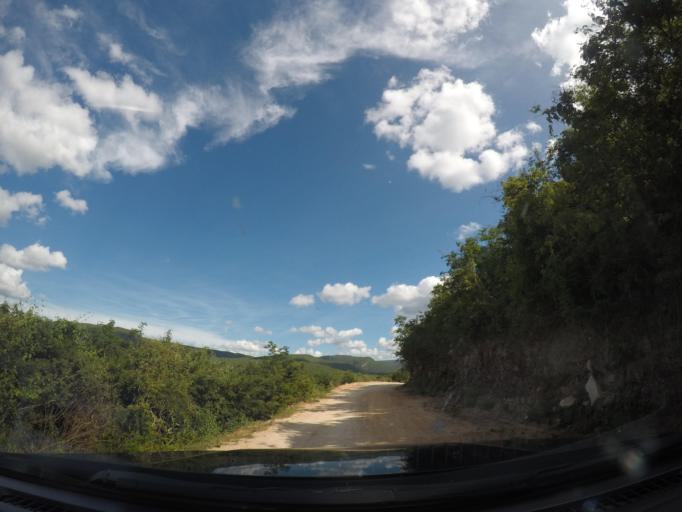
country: BR
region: Bahia
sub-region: Barra Da Estiva
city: Barra da Estiva
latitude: -13.2065
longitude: -41.5926
